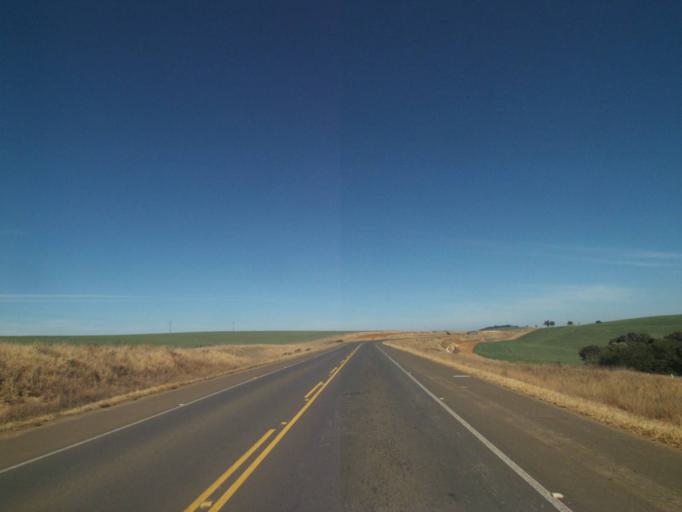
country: BR
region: Parana
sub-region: Tibagi
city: Tibagi
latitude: -24.6285
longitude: -50.4544
